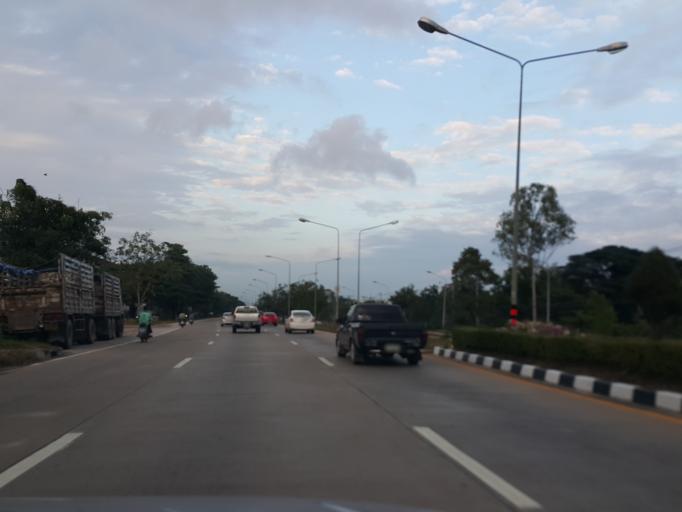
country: TH
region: Lampang
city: Lampang
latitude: 18.2548
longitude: 99.4571
